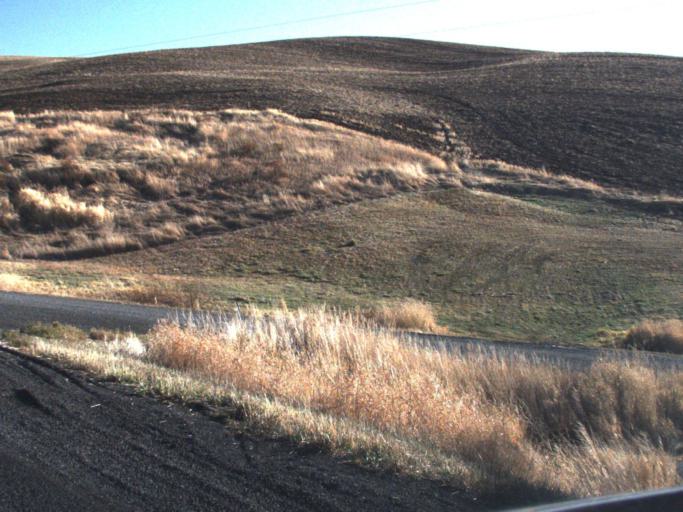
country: US
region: Washington
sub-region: Whitman County
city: Colfax
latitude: 46.7370
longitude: -117.3406
